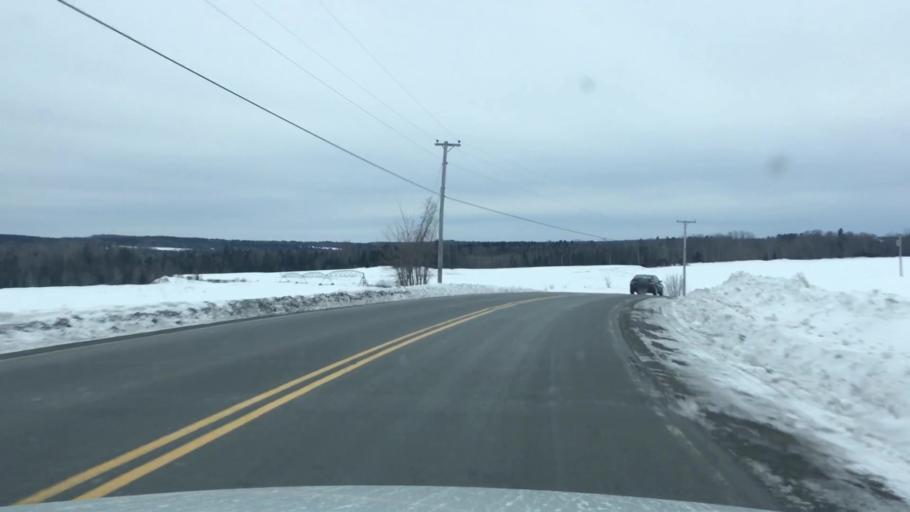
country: US
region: Maine
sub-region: Penobscot County
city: Garland
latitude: 44.9762
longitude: -69.0915
